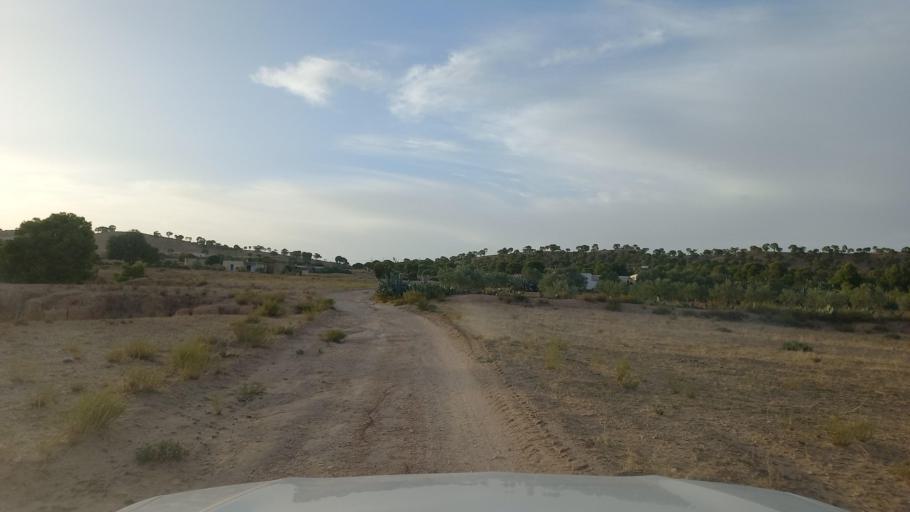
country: TN
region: Al Qasrayn
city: Sbiba
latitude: 35.4115
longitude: 8.9149
